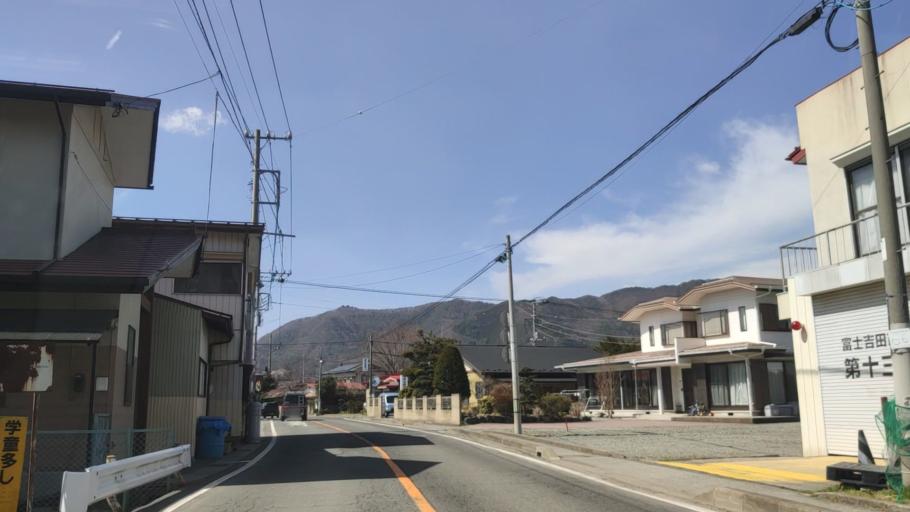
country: JP
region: Yamanashi
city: Fujikawaguchiko
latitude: 35.4922
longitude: 138.8119
